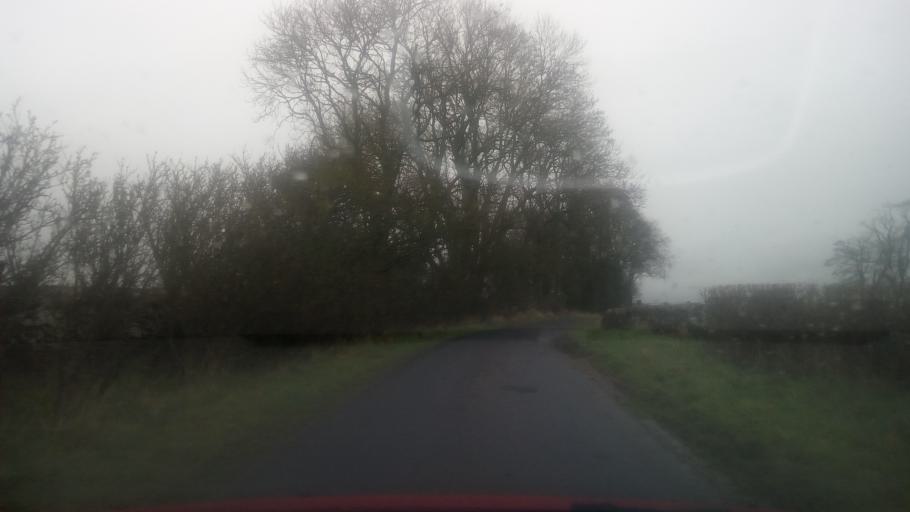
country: GB
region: Scotland
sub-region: The Scottish Borders
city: Saint Boswells
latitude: 55.6159
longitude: -2.5623
